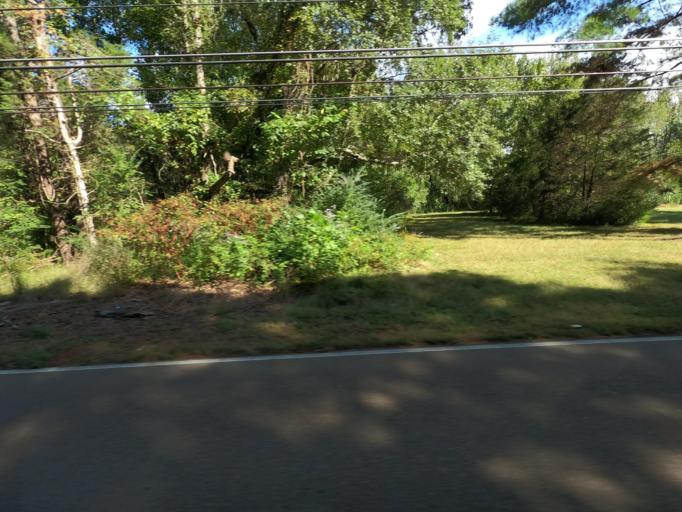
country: US
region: Tennessee
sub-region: Shelby County
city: Arlington
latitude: 35.2397
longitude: -89.6499
